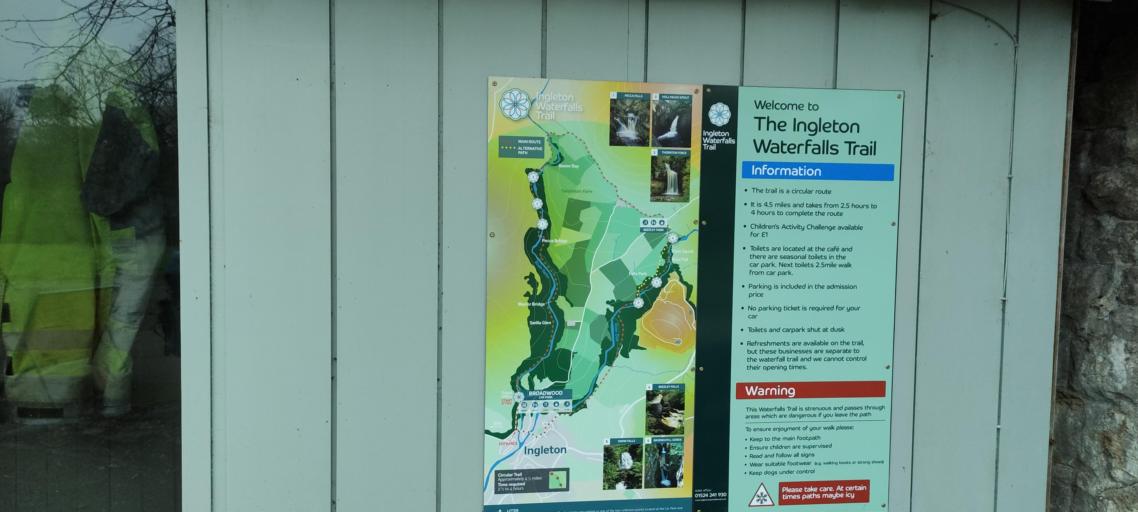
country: GB
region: England
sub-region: North Yorkshire
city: Ingleton
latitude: 54.1553
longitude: -2.4711
